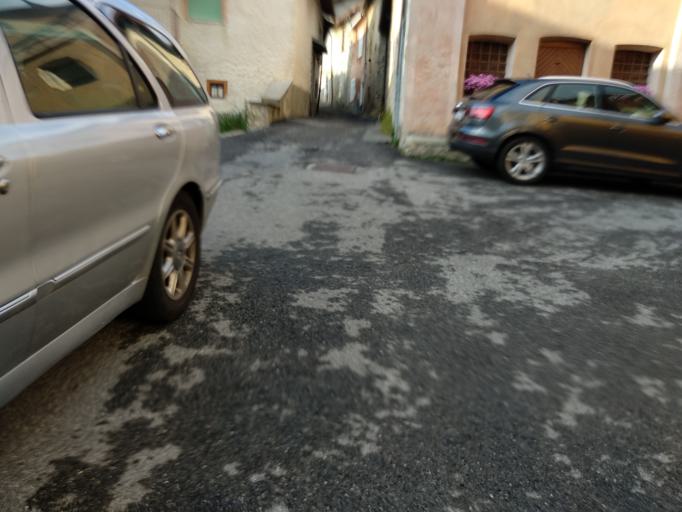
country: IT
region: Piedmont
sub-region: Provincia di Cuneo
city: Garessio
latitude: 44.1973
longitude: 8.0332
